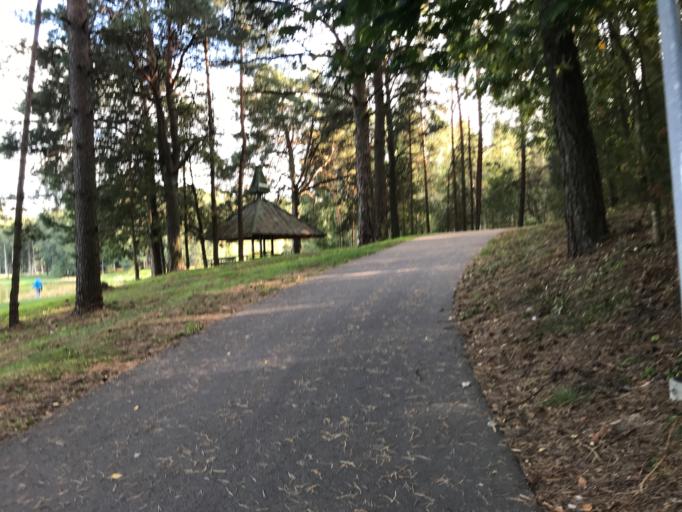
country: LT
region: Alytaus apskritis
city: Druskininkai
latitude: 54.0164
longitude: 23.9602
